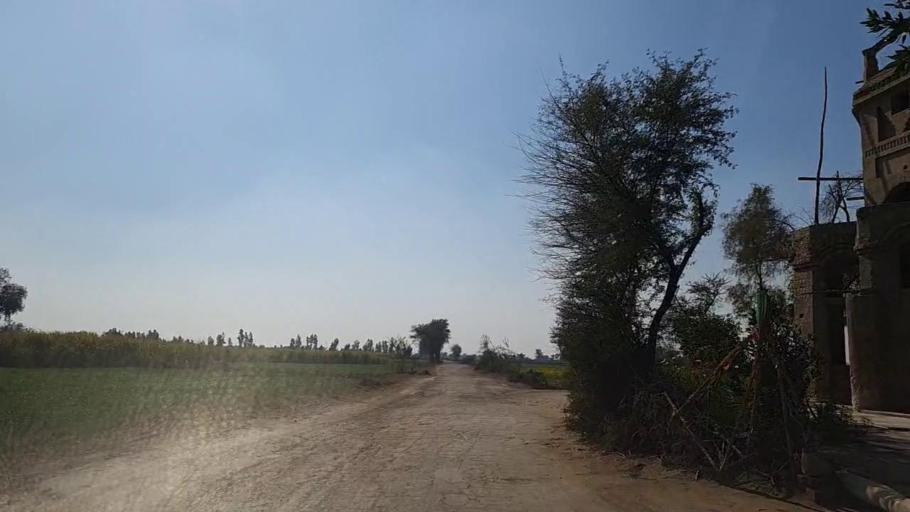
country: PK
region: Sindh
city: Bandhi
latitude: 26.5272
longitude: 68.2934
